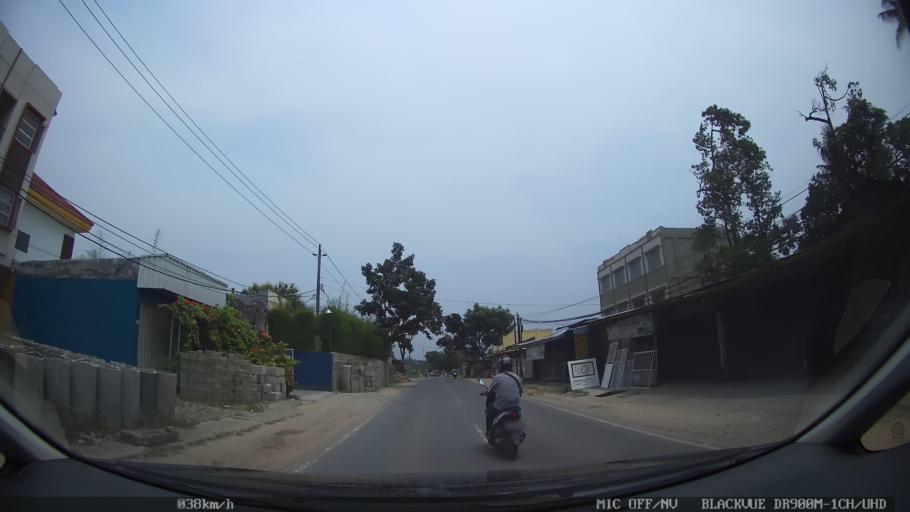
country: ID
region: Lampung
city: Kedaton
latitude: -5.4009
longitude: 105.3120
